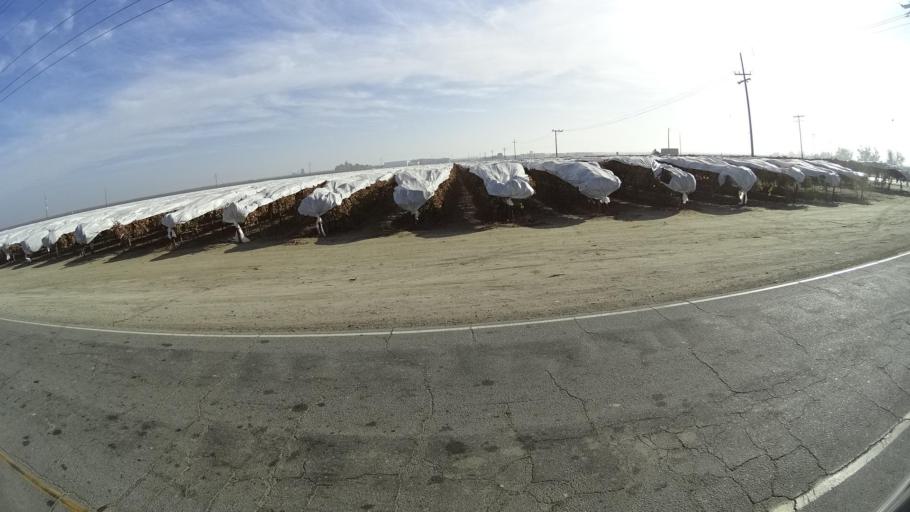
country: US
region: California
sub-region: Kern County
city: McFarland
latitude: 35.6025
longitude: -119.2043
